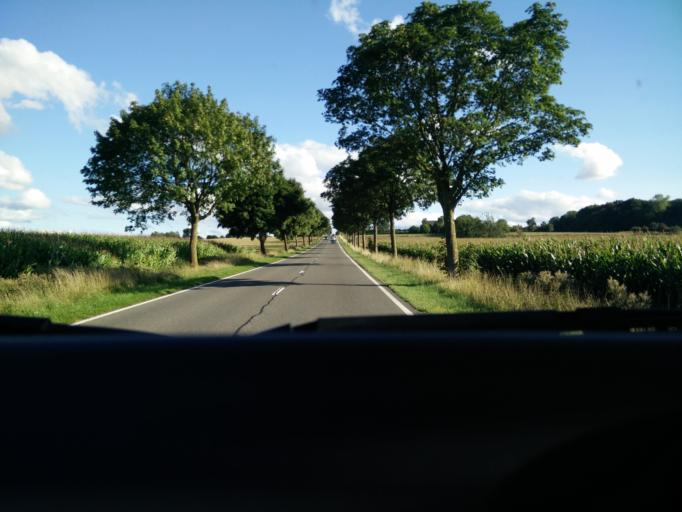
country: BE
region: Wallonia
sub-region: Province du Hainaut
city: Beaumont
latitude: 50.2682
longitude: 4.2152
